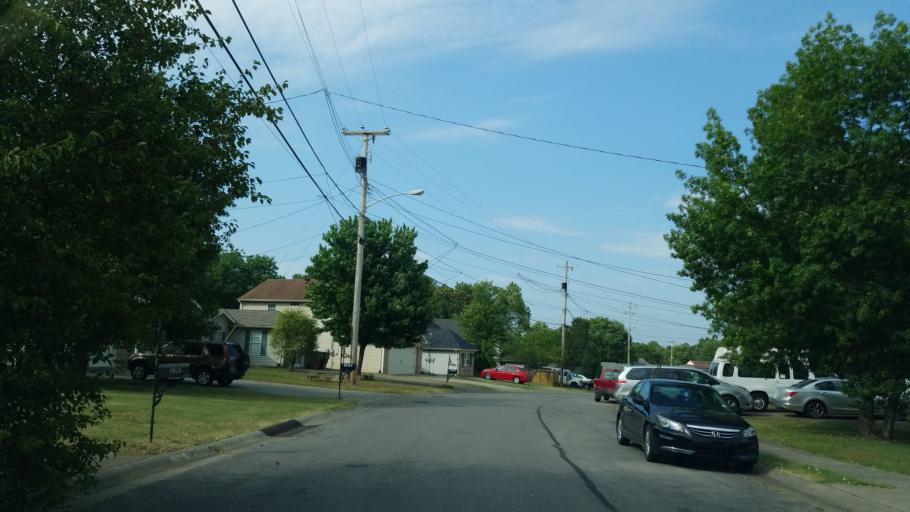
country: US
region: Tennessee
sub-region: Rutherford County
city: La Vergne
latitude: 36.0419
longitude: -86.5829
